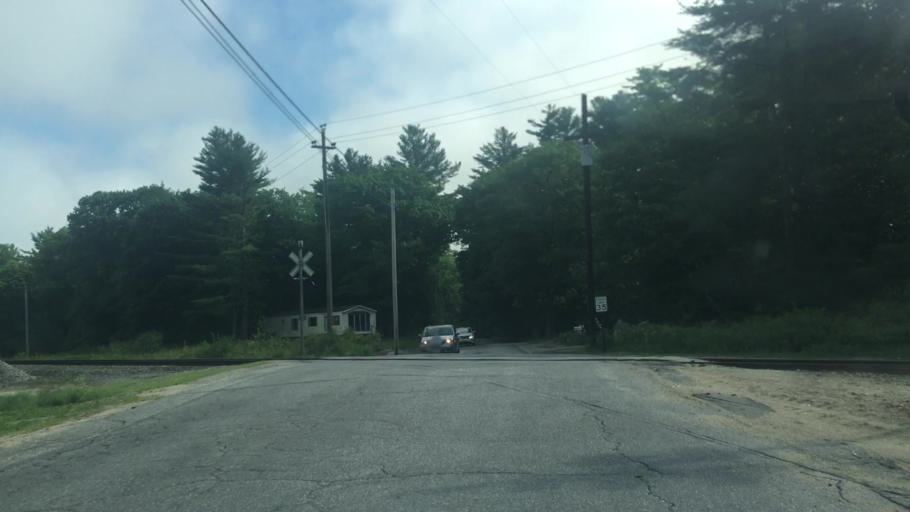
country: US
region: Maine
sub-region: Oxford County
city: South Paris
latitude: 44.1890
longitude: -70.5172
